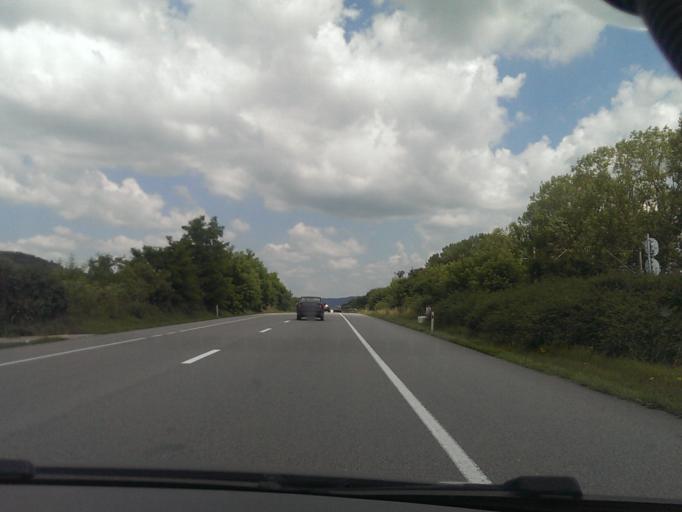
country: RO
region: Cluj
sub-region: Comuna Bontida
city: Rascruci
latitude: 46.8707
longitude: 23.7687
